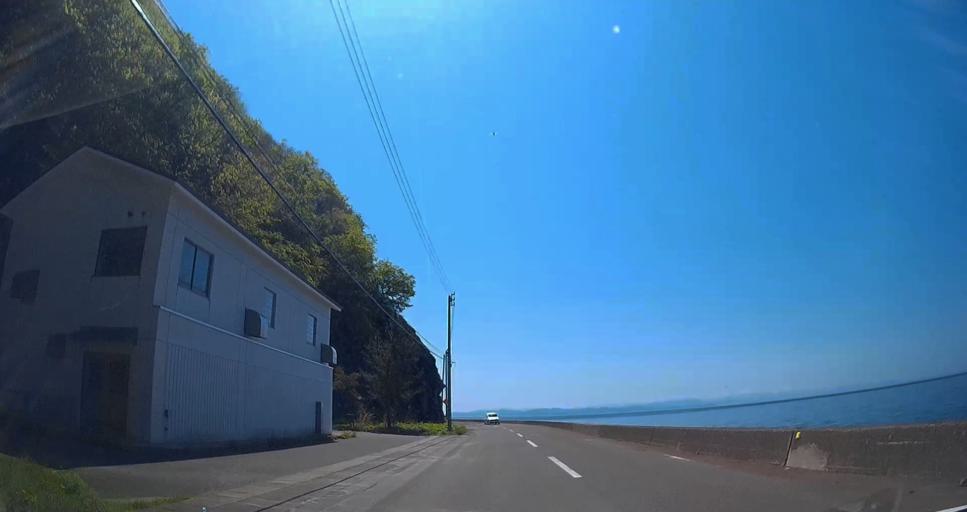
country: JP
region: Aomori
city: Aomori Shi
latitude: 41.1306
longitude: 140.7963
